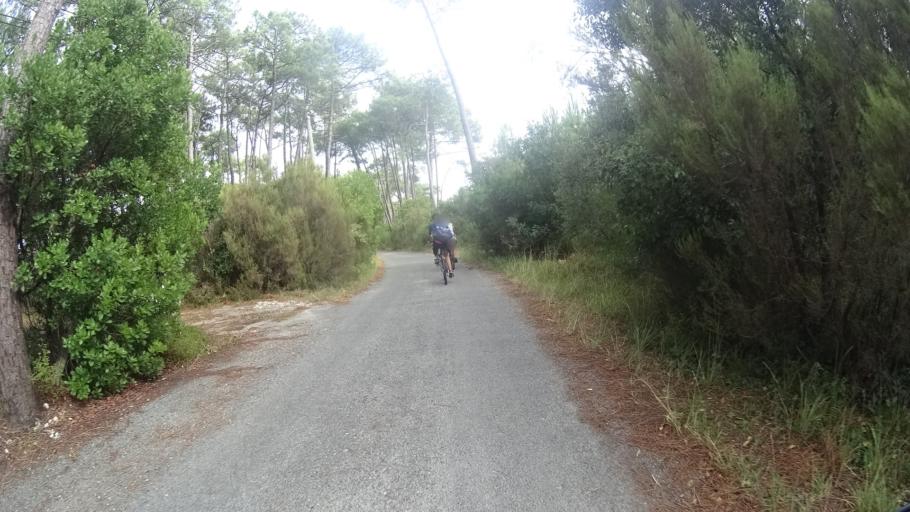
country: FR
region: Aquitaine
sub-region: Departement de la Gironde
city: Lacanau
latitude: 44.9912
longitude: -1.1448
